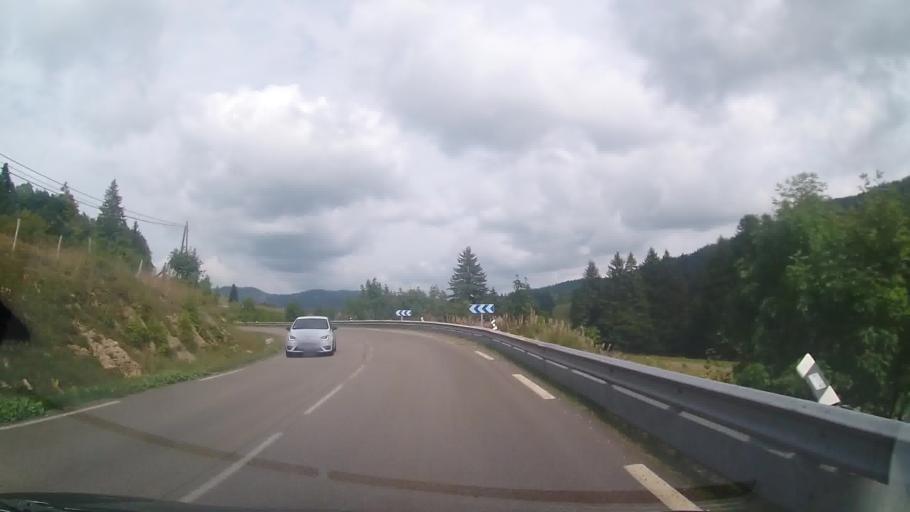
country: FR
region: Franche-Comte
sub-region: Departement du Jura
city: Les Rousses
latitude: 46.4356
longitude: 6.0771
